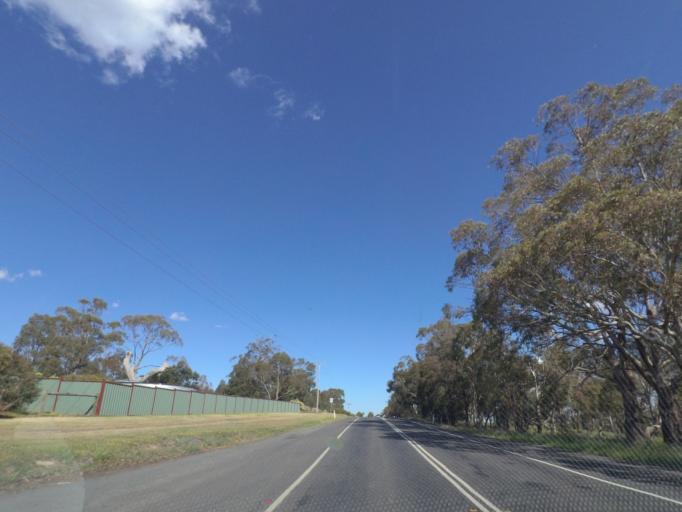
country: AU
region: Victoria
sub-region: Moorabool
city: Bacchus Marsh
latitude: -37.5712
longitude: 144.3134
